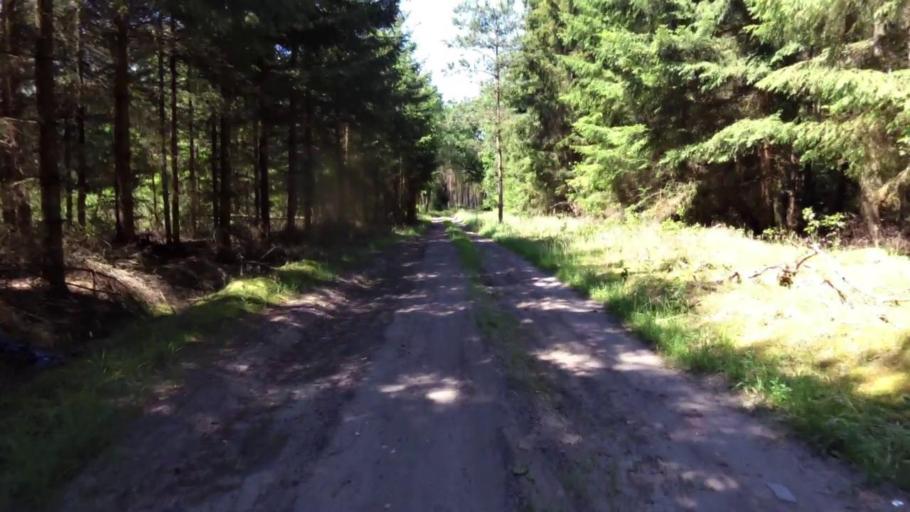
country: PL
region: West Pomeranian Voivodeship
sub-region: Powiat bialogardzki
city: Bialogard
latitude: 53.9541
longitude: 16.1009
